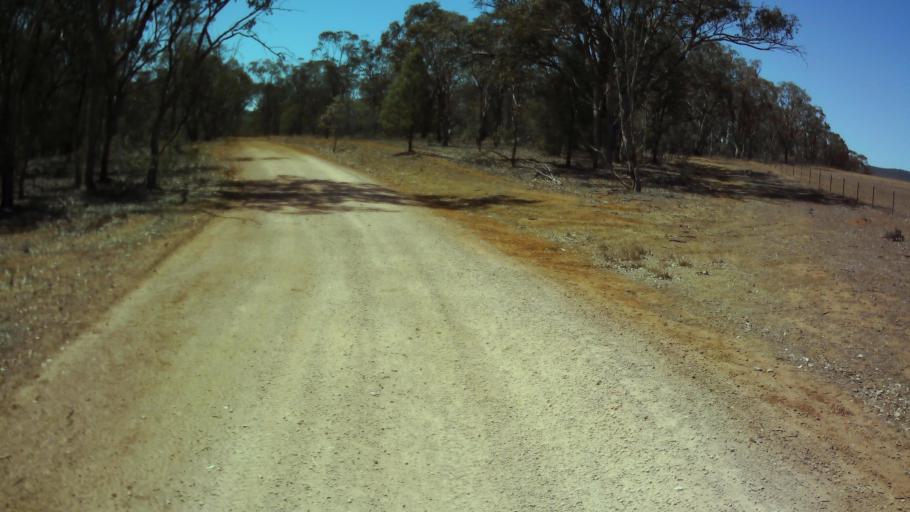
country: AU
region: New South Wales
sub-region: Weddin
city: Grenfell
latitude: -33.9454
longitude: 148.0802
